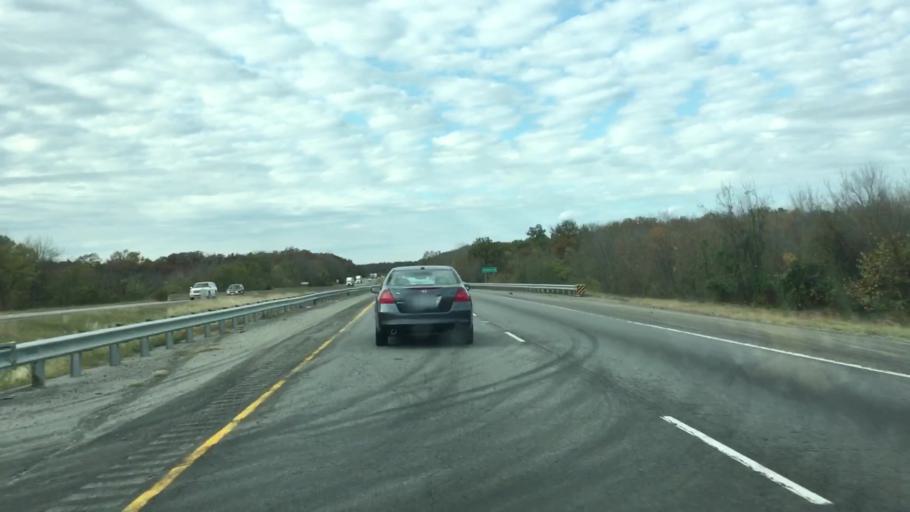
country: US
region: Arkansas
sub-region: Faulkner County
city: Conway
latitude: 35.1293
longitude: -92.5134
